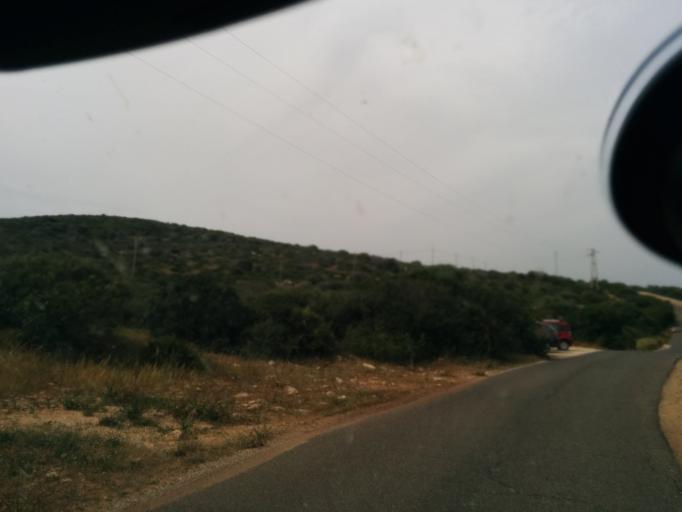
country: IT
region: Sardinia
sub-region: Provincia di Carbonia-Iglesias
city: Sant'Antioco
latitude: 39.0099
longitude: 8.4486
